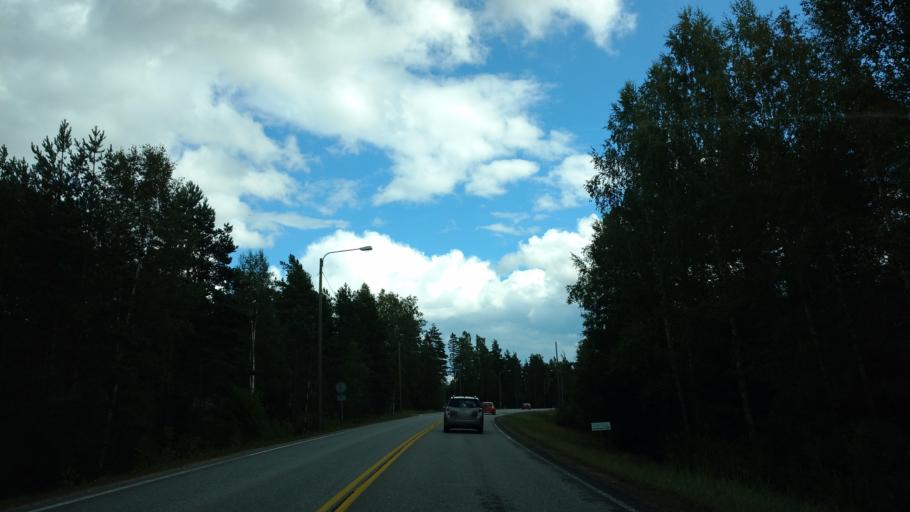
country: FI
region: Uusimaa
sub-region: Helsinki
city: Karjalohja
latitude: 60.2105
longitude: 23.6651
